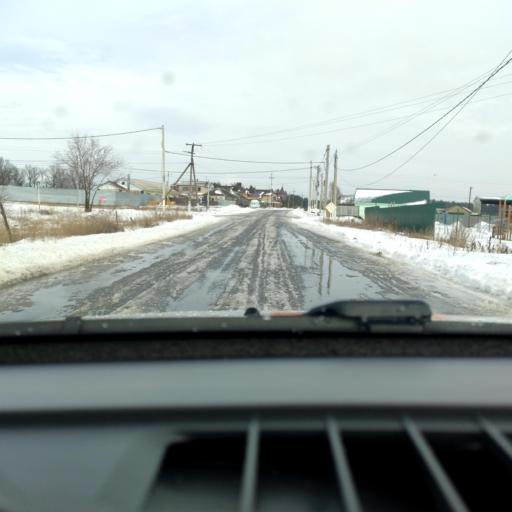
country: RU
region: Voronezj
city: Podgornoye
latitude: 51.7732
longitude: 39.1247
